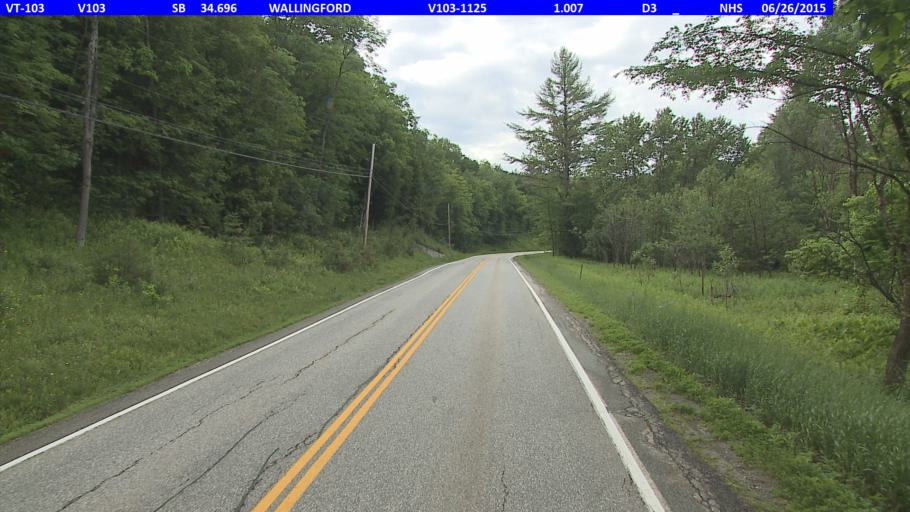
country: US
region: Vermont
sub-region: Rutland County
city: Rutland
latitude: 43.4645
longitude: -72.8740
